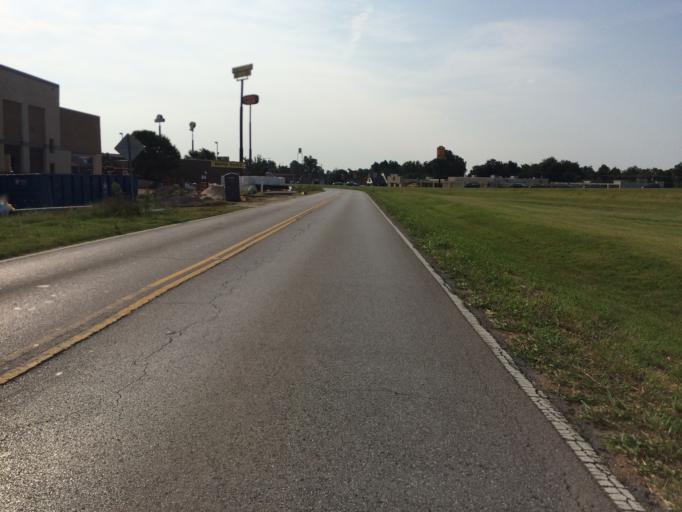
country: US
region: Oklahoma
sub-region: Cleveland County
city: Norman
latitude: 35.2198
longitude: -97.4838
